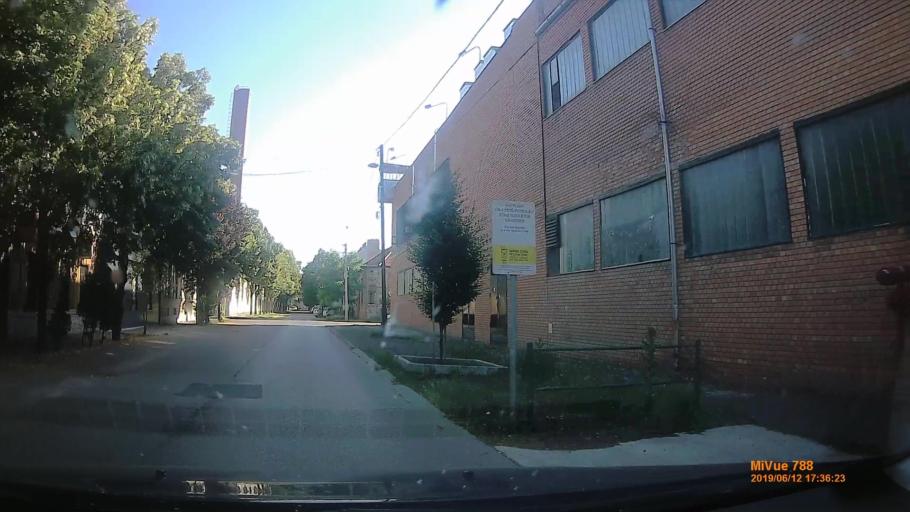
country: HU
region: Csongrad
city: Szeged
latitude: 46.2587
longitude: 20.1371
